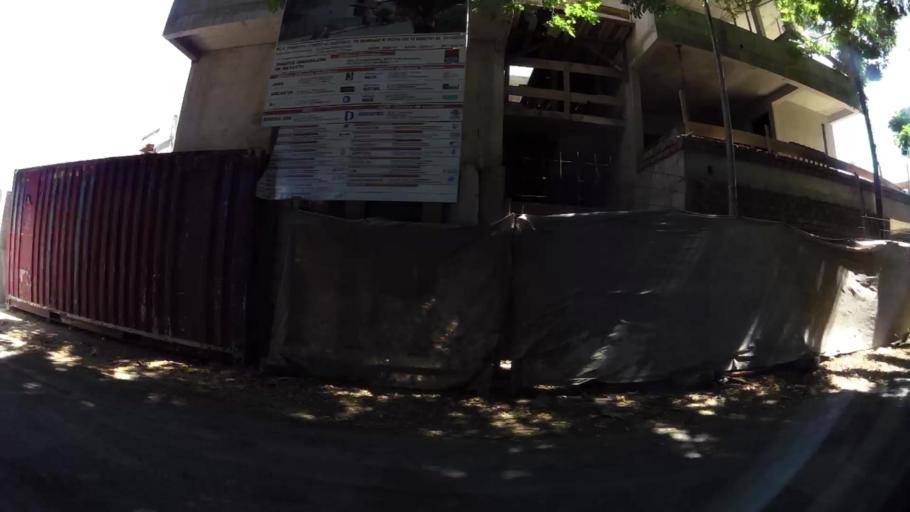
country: YT
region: Pamandzi
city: Pamandzi
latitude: -12.7955
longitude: 45.2791
